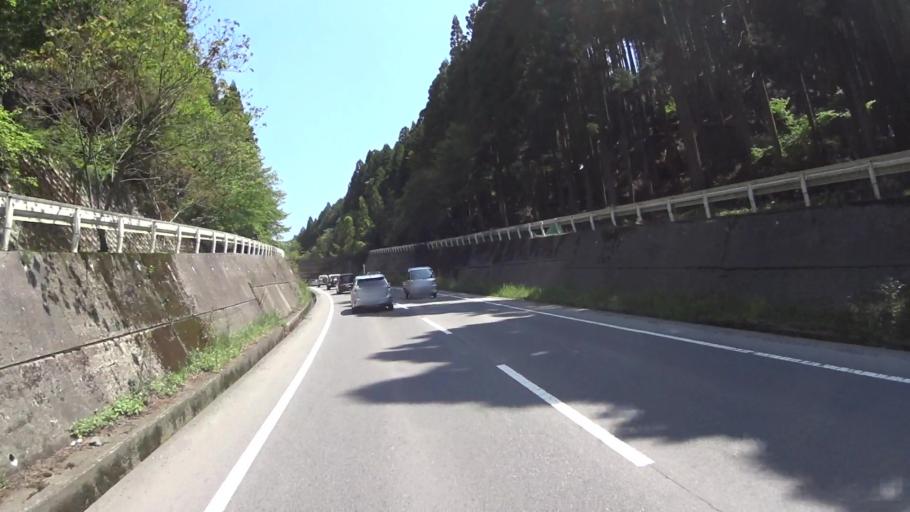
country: JP
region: Shiga Prefecture
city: Kitahama
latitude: 35.1585
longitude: 135.8518
